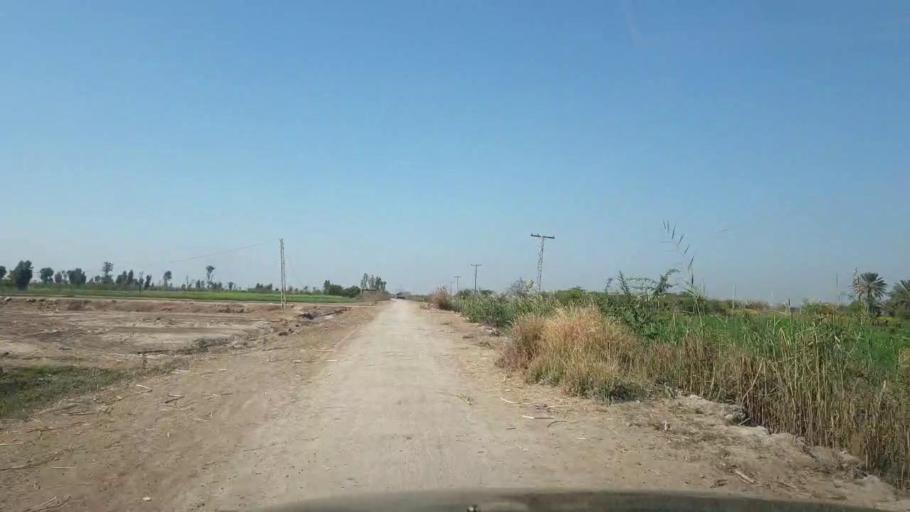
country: PK
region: Sindh
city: Mirpur Khas
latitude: 25.5978
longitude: 69.0659
